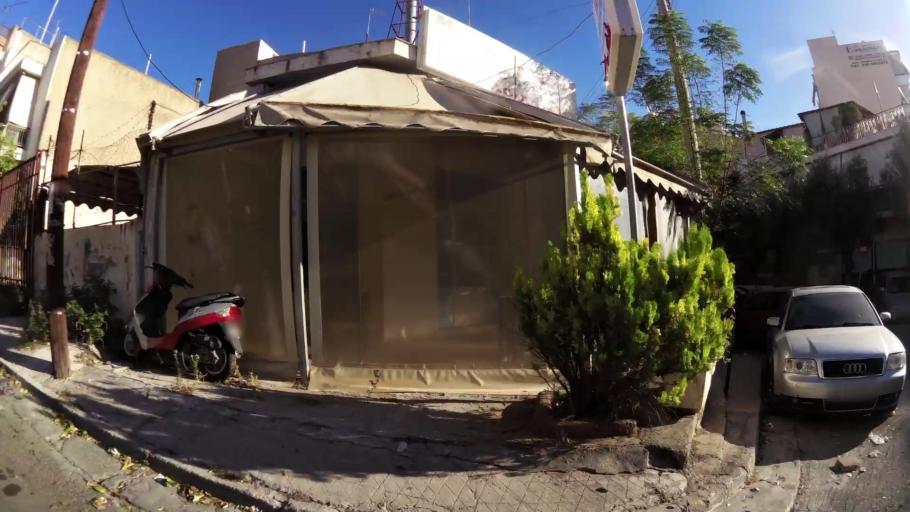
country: GR
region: Attica
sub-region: Nomos Piraios
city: Agios Ioannis Rentis
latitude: 37.9762
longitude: 23.6590
